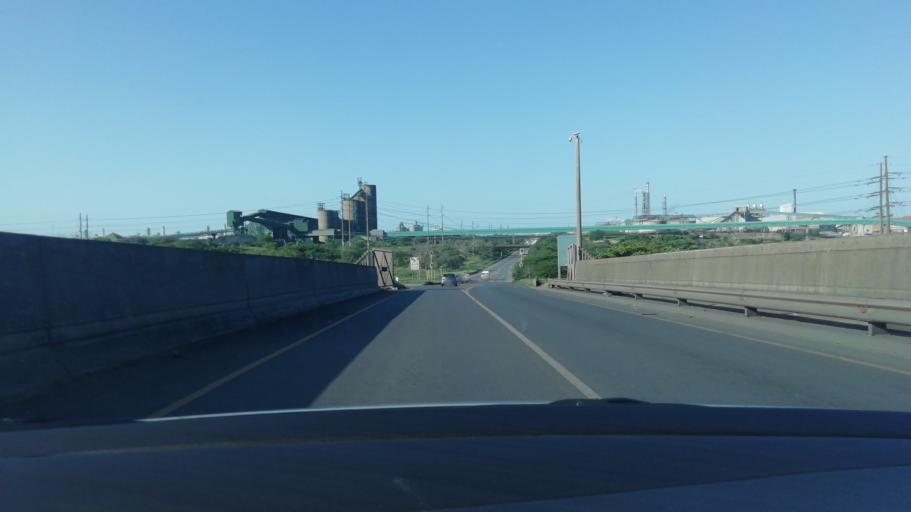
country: ZA
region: KwaZulu-Natal
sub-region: uThungulu District Municipality
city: Richards Bay
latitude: -28.7822
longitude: 32.0281
